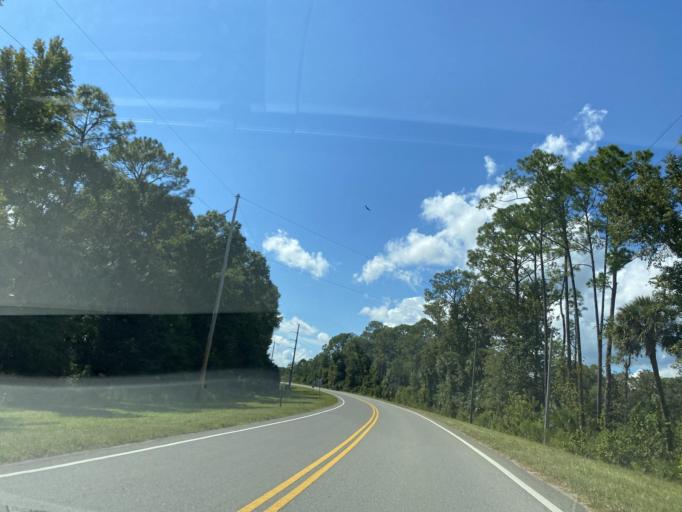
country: US
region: Florida
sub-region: Lake County
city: Umatilla
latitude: 28.9622
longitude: -81.5954
